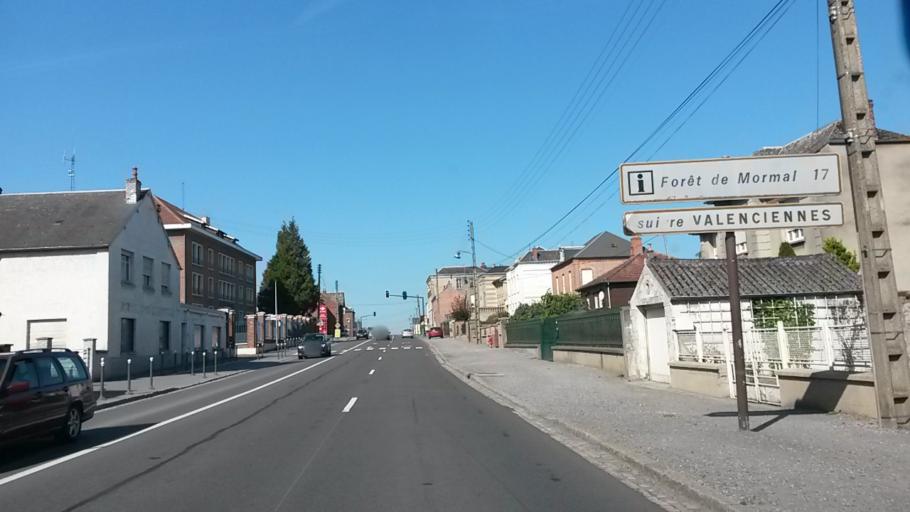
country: FR
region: Nord-Pas-de-Calais
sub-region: Departement du Nord
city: Avesnes-sur-Helpe
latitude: 50.1193
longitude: 3.9280
